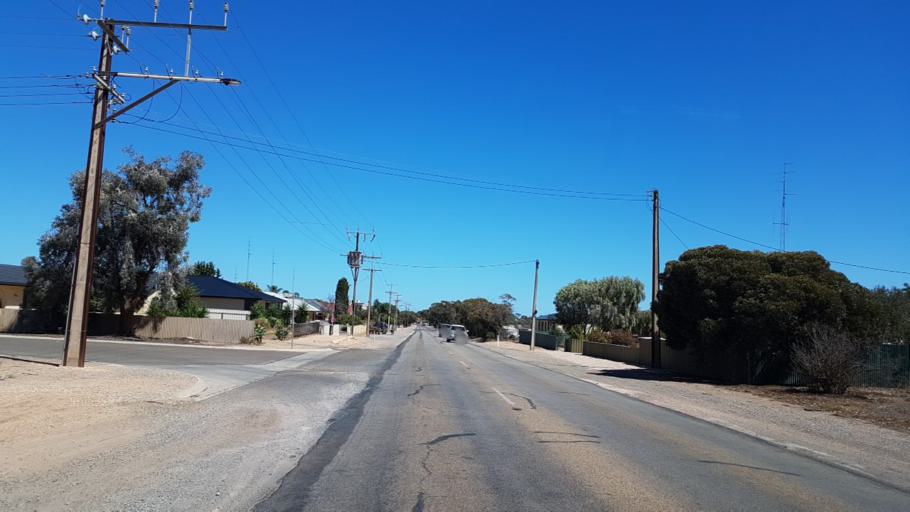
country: AU
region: South Australia
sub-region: Copper Coast
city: Wallaroo
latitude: -33.9374
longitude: 137.6444
